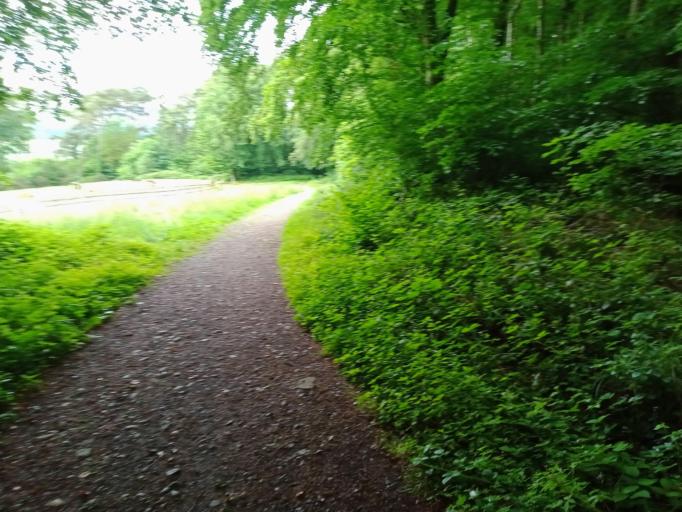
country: IE
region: Leinster
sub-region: Laois
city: Stradbally
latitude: 53.0043
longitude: -7.1267
